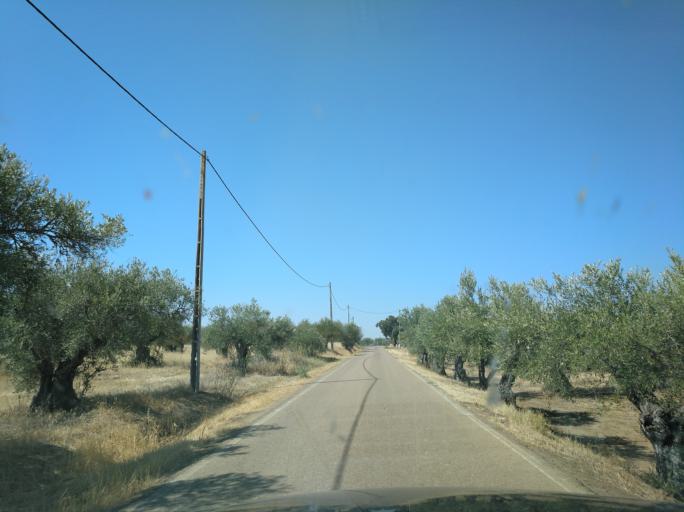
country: PT
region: Portalegre
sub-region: Campo Maior
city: Campo Maior
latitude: 39.0330
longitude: -7.0417
